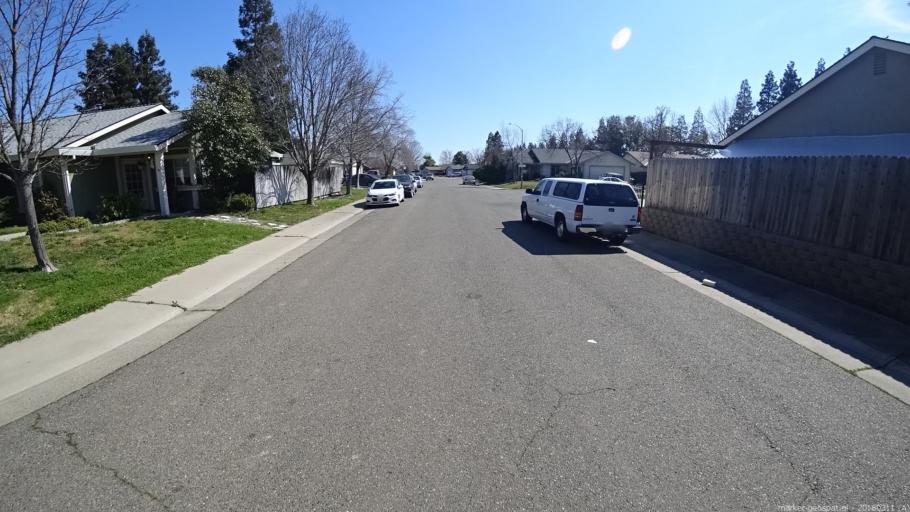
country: US
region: California
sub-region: Sacramento County
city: Florin
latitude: 38.4607
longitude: -121.3908
